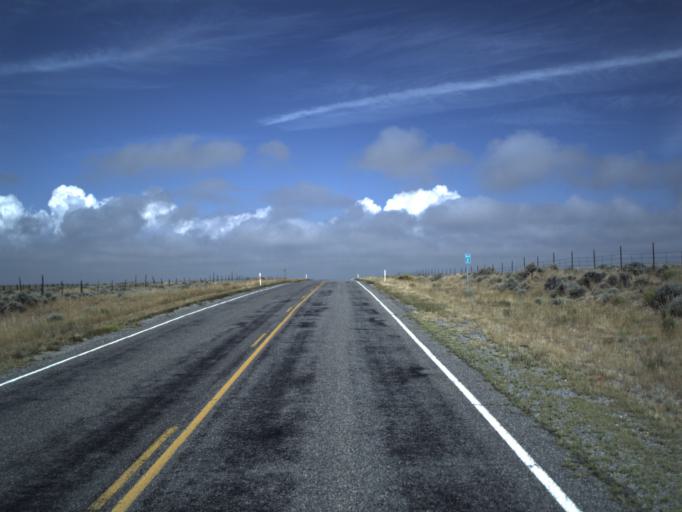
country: US
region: Wyoming
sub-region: Uinta County
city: Evanston
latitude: 41.4365
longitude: -111.0680
